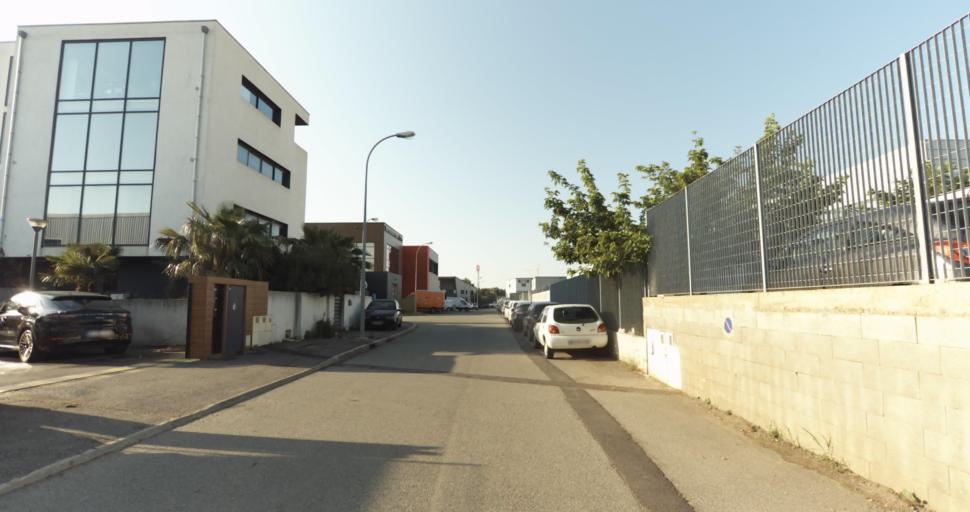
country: FR
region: Corsica
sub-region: Departement de la Haute-Corse
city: Biguglia
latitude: 42.5961
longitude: 9.4413
